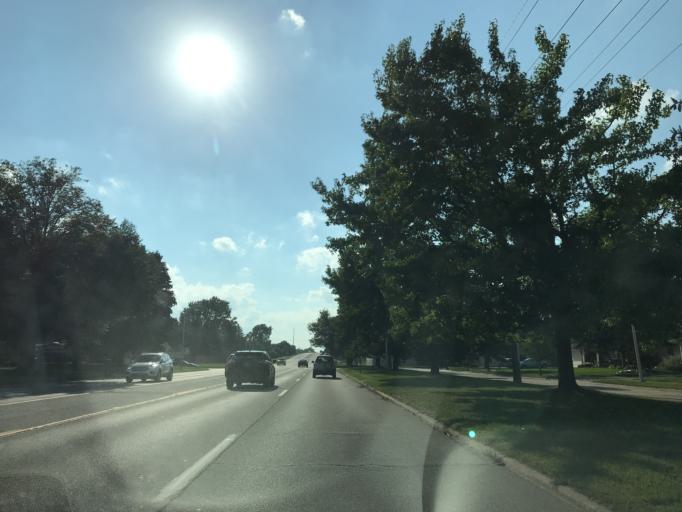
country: US
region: Michigan
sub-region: Wayne County
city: Plymouth
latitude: 42.3961
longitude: -83.4251
